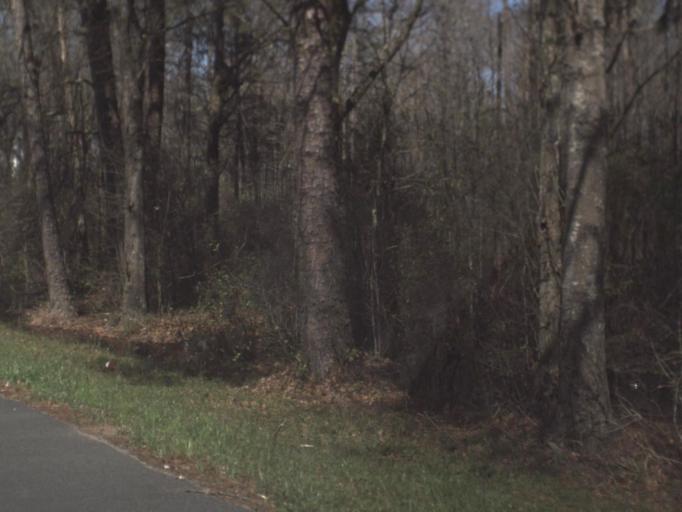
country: US
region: Florida
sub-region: Gadsden County
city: Gretna
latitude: 30.6451
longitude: -84.6786
